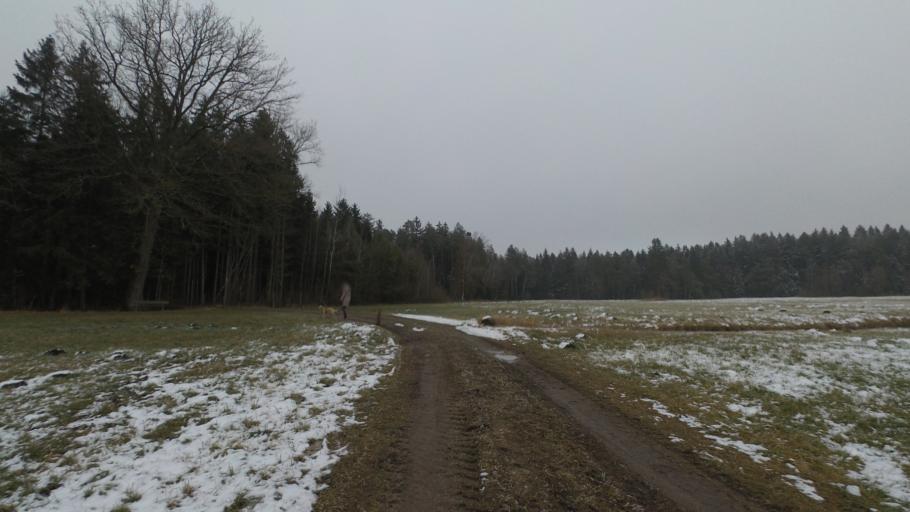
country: DE
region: Bavaria
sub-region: Upper Bavaria
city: Nussdorf
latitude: 47.8992
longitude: 12.5767
